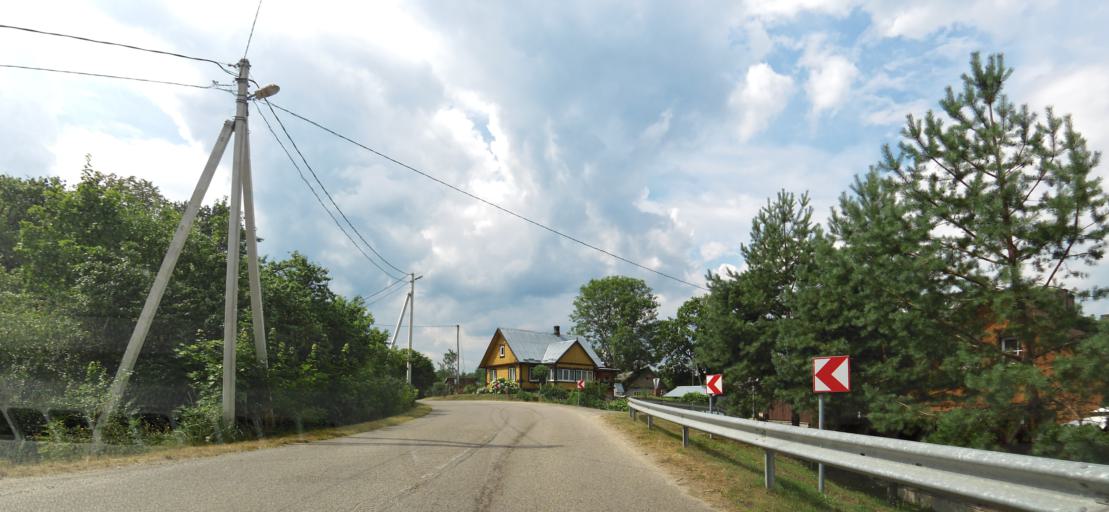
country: LT
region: Alytaus apskritis
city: Druskininkai
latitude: 53.9880
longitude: 24.0982
